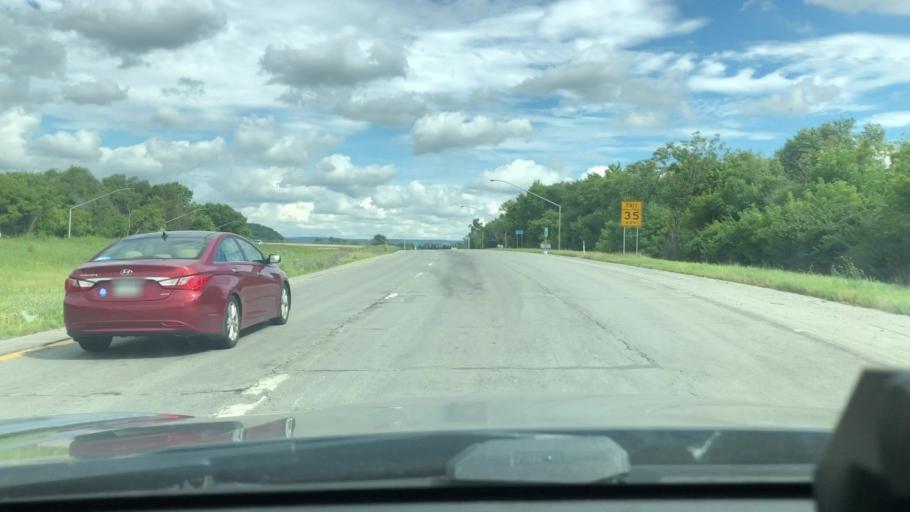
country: US
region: Pennsylvania
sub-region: Northampton County
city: Tatamy
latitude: 40.7512
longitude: -75.2649
